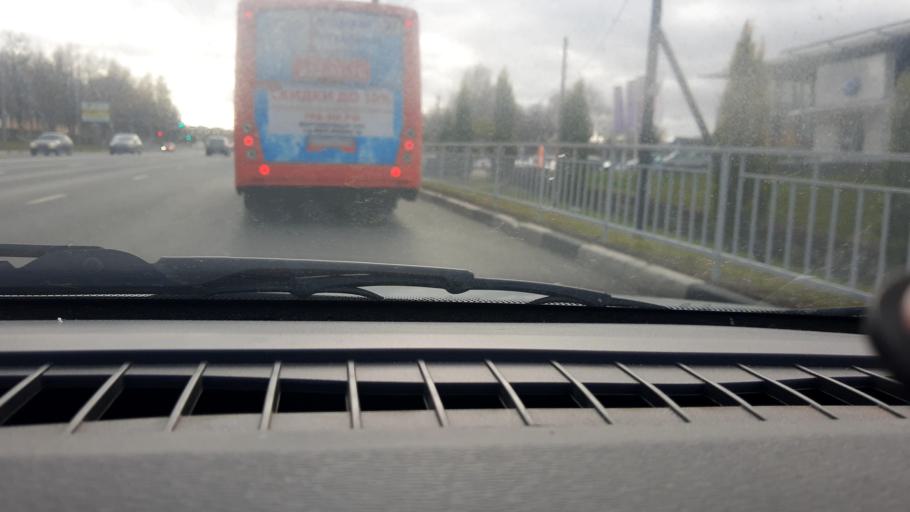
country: RU
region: Nizjnij Novgorod
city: Nizhniy Novgorod
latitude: 56.2482
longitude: 43.9663
